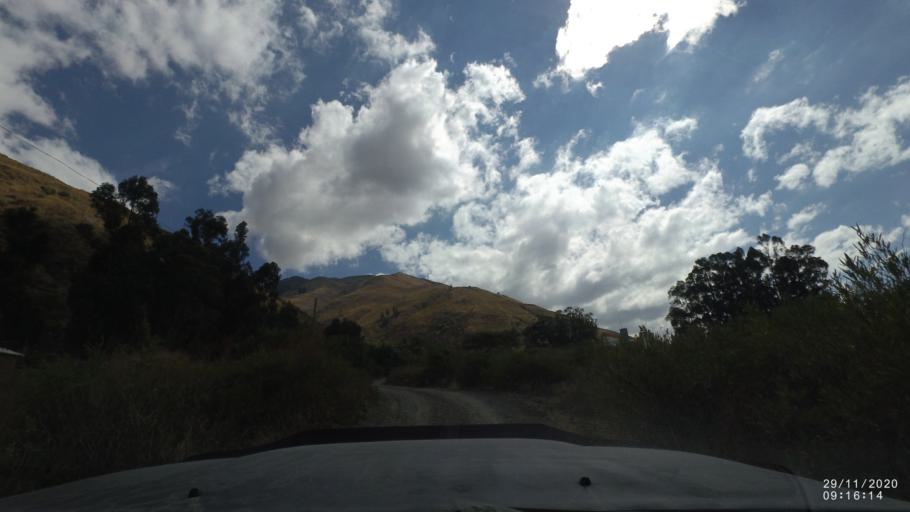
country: BO
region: Cochabamba
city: Cochabamba
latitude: -17.3270
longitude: -66.1872
